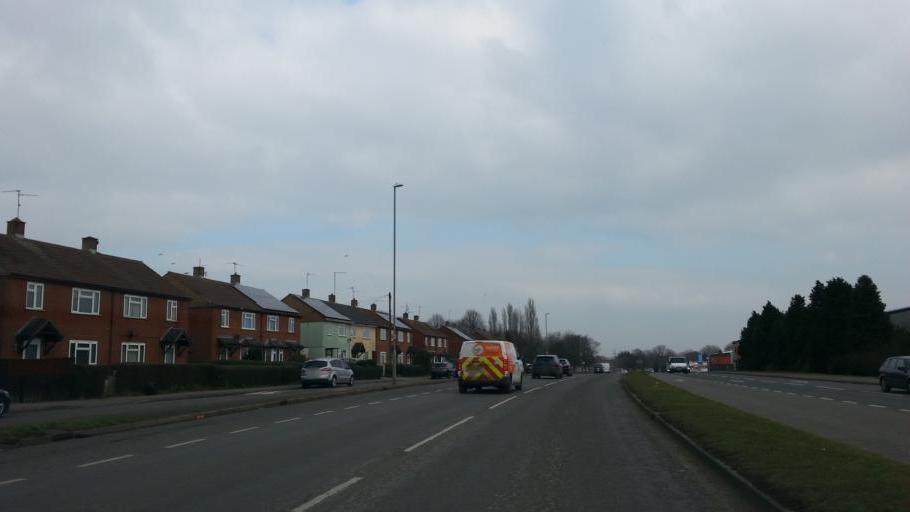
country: GB
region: England
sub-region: Northamptonshire
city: Corby
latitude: 52.4882
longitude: -0.6847
